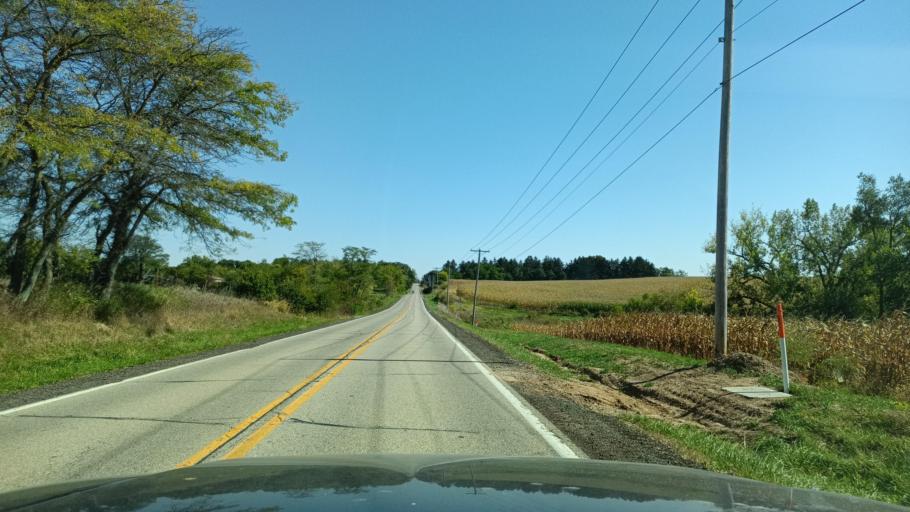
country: US
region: Illinois
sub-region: McLean County
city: Danvers
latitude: 40.6168
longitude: -89.2300
